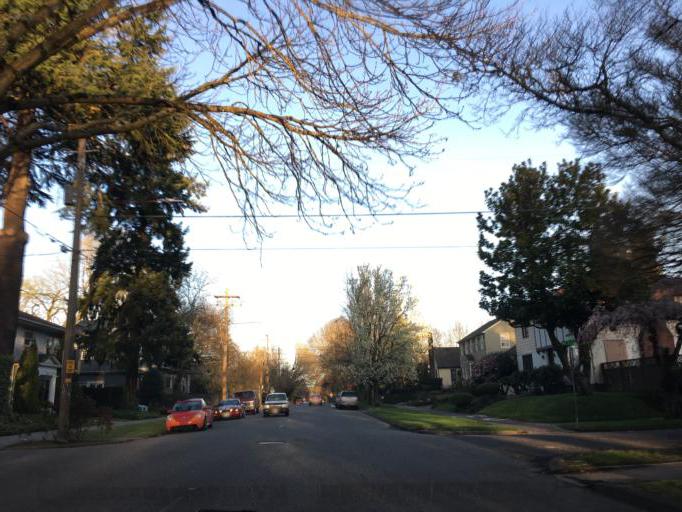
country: US
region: Oregon
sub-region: Multnomah County
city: Portland
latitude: 45.5421
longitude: -122.6426
